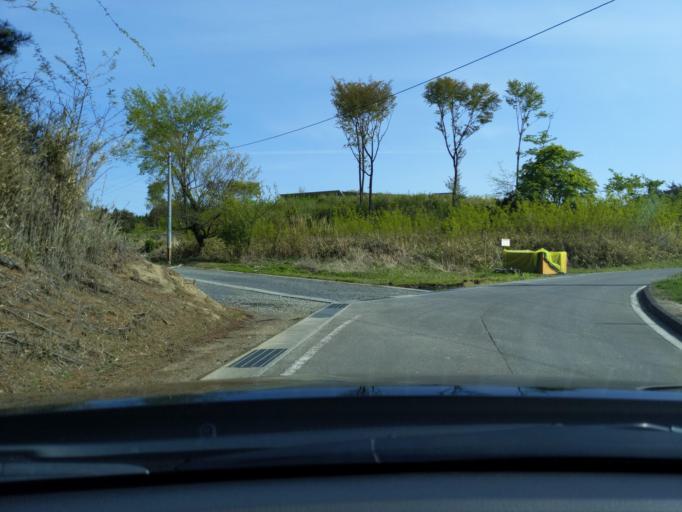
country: JP
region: Fukushima
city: Sukagawa
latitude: 37.3141
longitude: 140.4239
